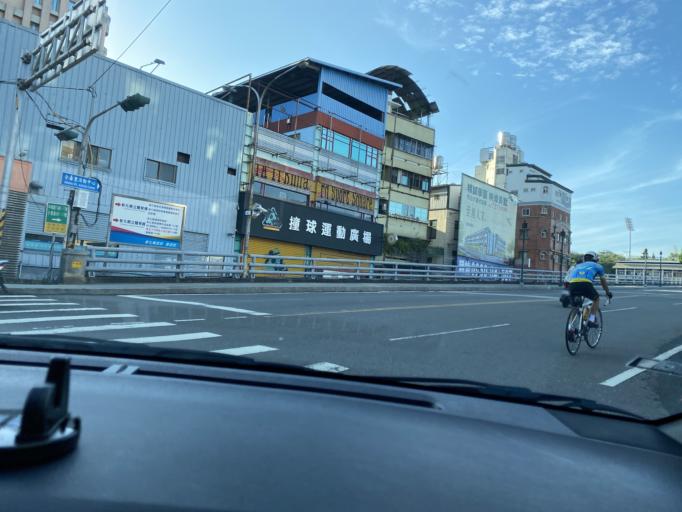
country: TW
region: Taiwan
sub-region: Changhua
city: Chang-hua
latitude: 24.0707
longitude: 120.5524
